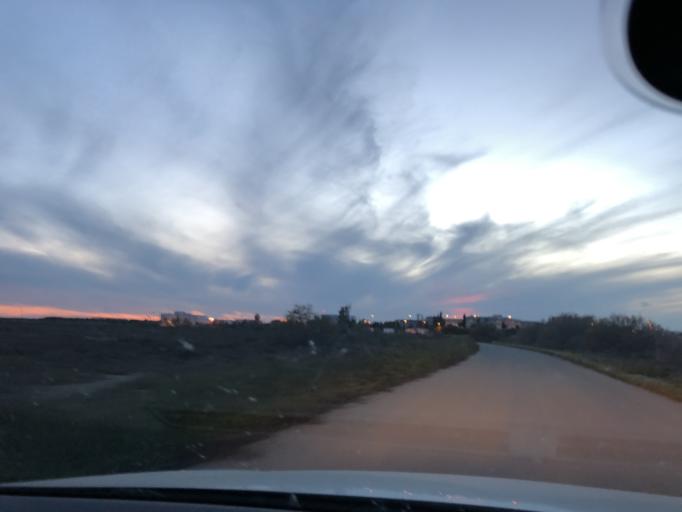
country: CY
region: Larnaka
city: Meneou
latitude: 34.8690
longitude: 33.6355
